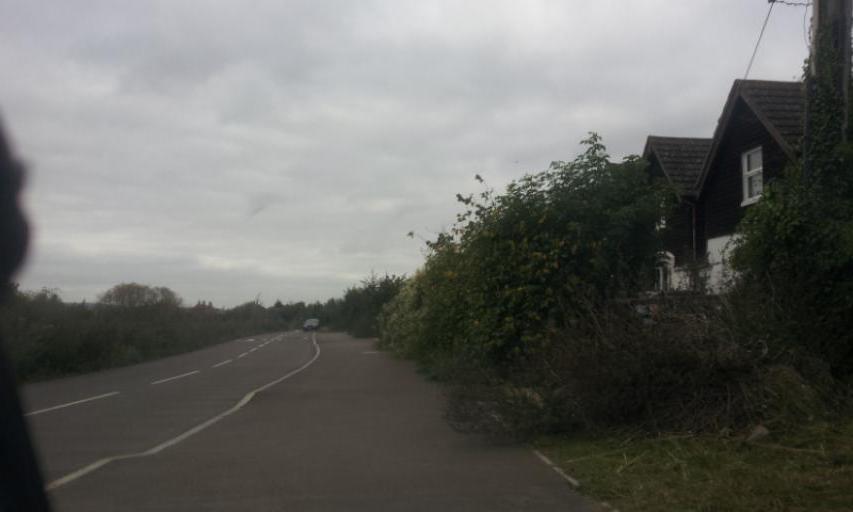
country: GB
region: England
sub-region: Medway
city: Halling
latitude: 51.3431
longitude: 0.4579
